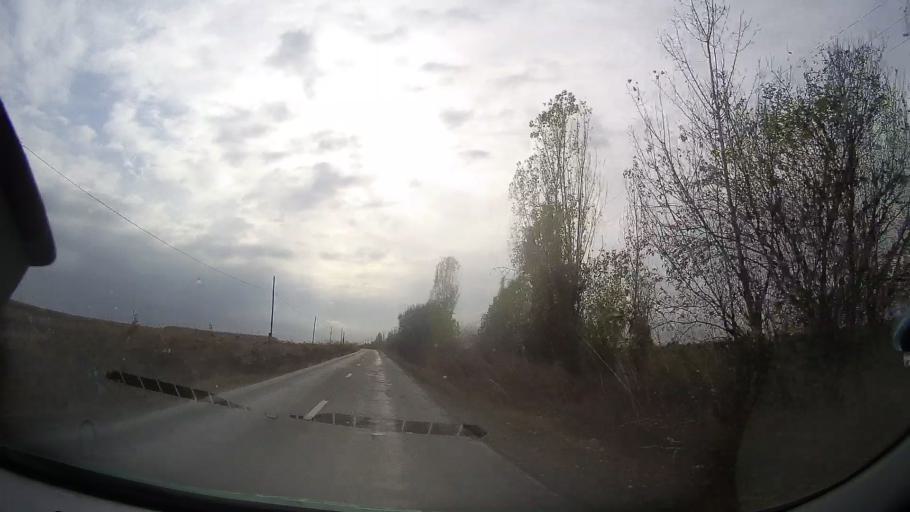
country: RO
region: Ialomita
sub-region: Comuna Maia
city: Maia
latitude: 44.7250
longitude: 26.3922
